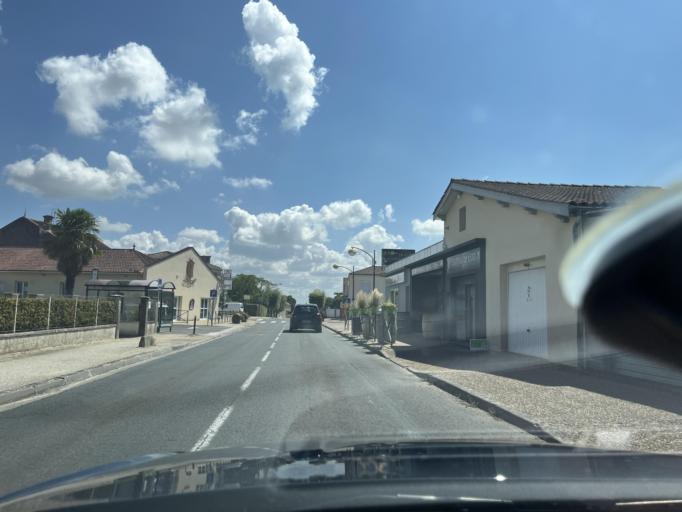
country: FR
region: Aquitaine
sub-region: Departement de la Gironde
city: Cantenac
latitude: 45.0640
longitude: -0.6172
